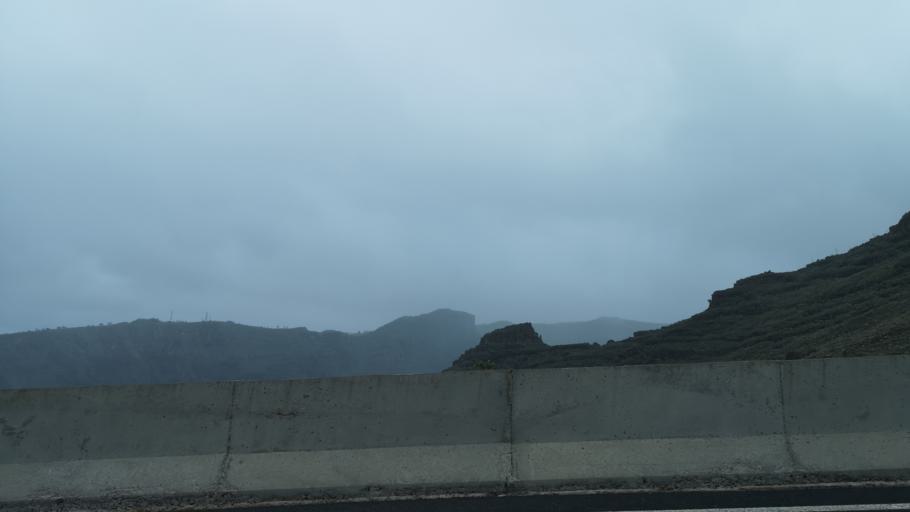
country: ES
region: Canary Islands
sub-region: Provincia de Santa Cruz de Tenerife
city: Alajero
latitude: 28.0631
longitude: -17.2037
